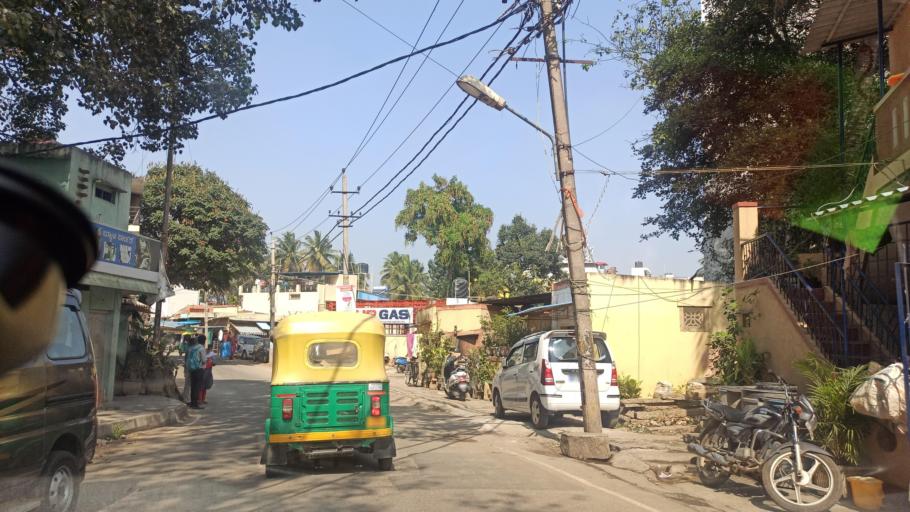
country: IN
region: Karnataka
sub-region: Bangalore Urban
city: Yelahanka
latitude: 13.0403
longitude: 77.5917
